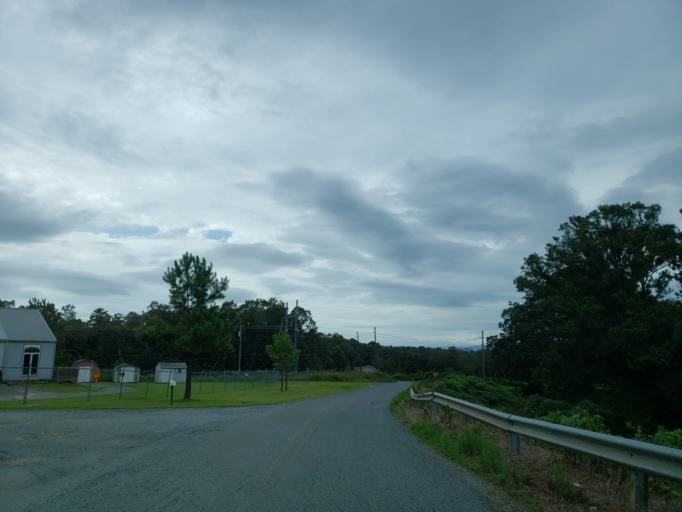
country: US
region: Georgia
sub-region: Gilmer County
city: Ellijay
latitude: 34.6412
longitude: -84.5013
